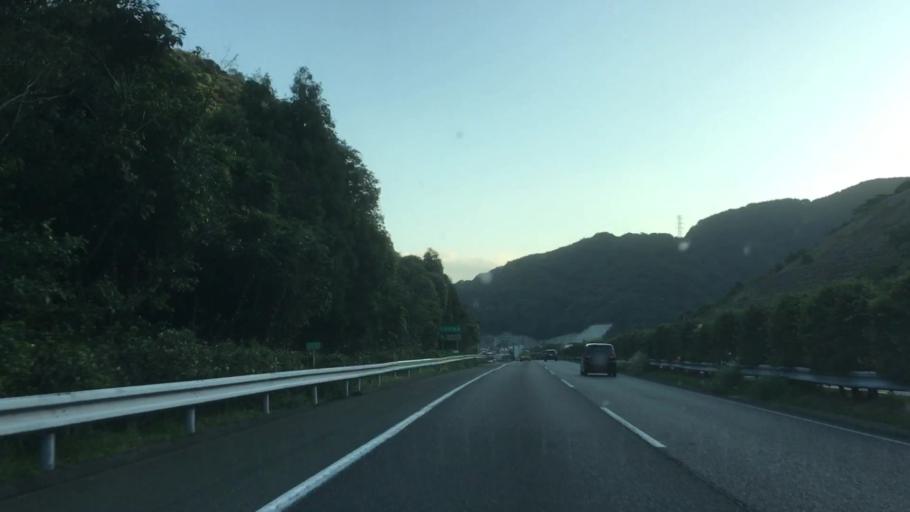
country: JP
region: Yamaguchi
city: Shimonoseki
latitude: 33.8926
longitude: 130.9714
